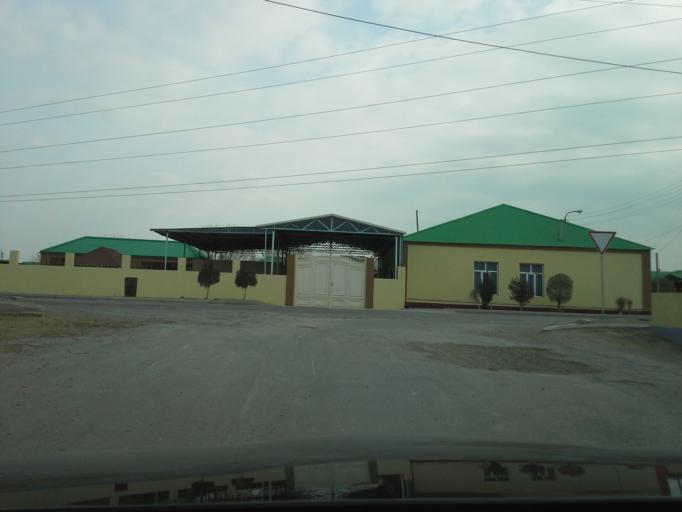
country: TM
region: Ahal
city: Abadan
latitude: 38.0375
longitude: 58.2542
